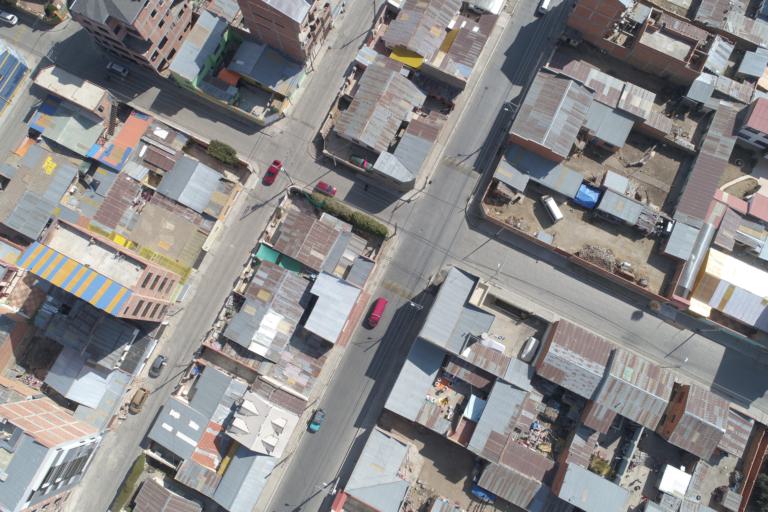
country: BO
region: La Paz
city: La Paz
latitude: -16.5301
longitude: -68.1498
